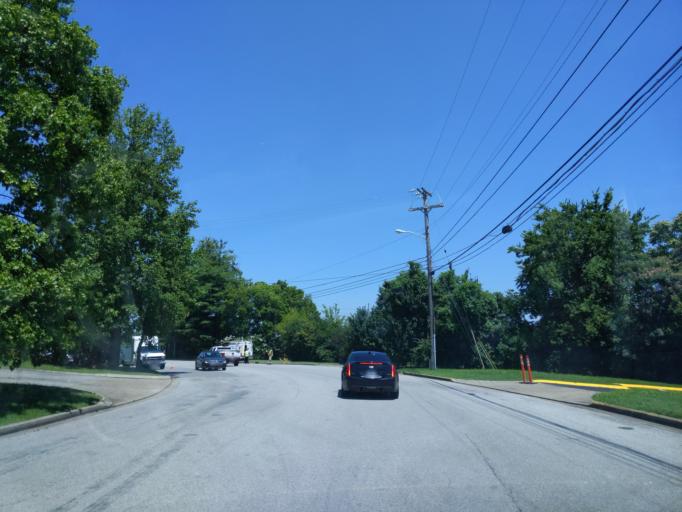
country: US
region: Tennessee
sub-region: Davidson County
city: Nashville
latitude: 36.1487
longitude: -86.7422
